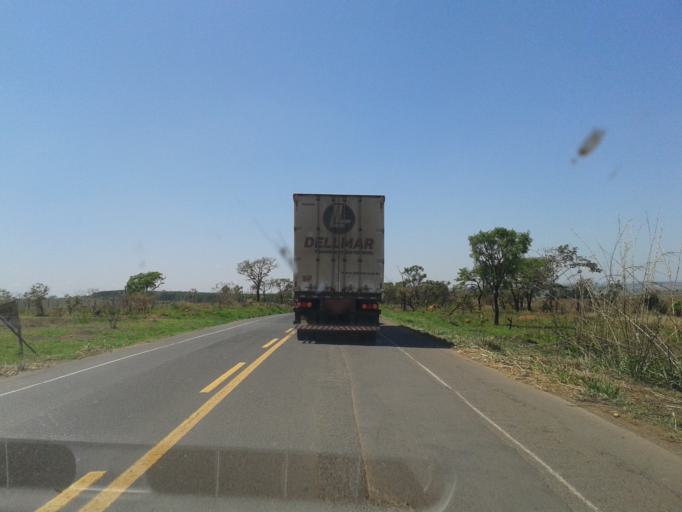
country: BR
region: Minas Gerais
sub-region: Araxa
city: Araxa
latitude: -19.4334
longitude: -47.2191
